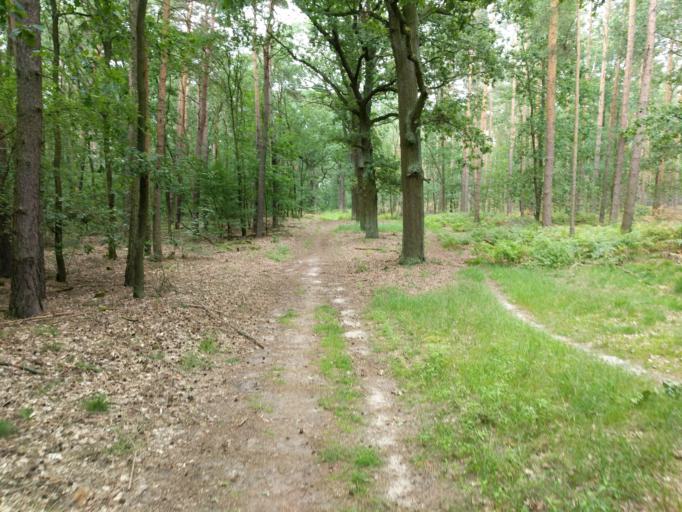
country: DE
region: Berlin
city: Gatow
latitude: 52.4950
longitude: 13.2124
